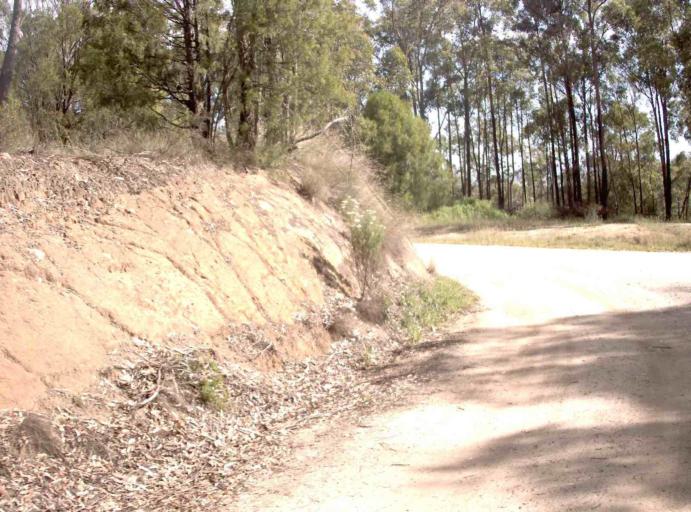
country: AU
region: Victoria
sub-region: East Gippsland
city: Lakes Entrance
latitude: -37.5266
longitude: 148.1584
